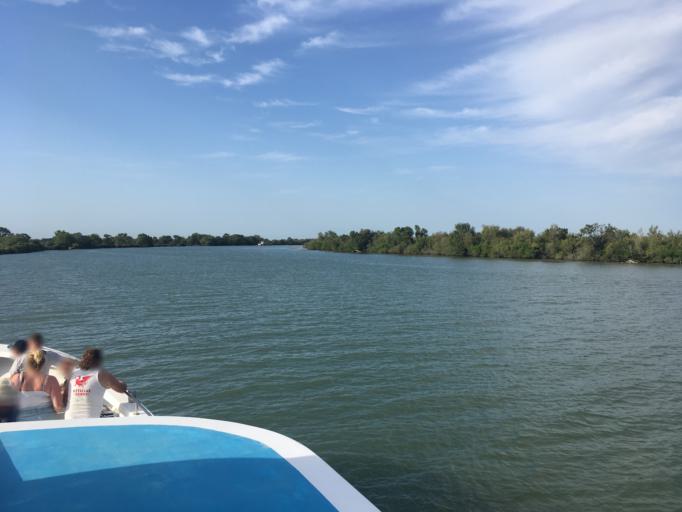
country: FR
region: Provence-Alpes-Cote d'Azur
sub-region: Departement des Bouches-du-Rhone
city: Saintes-Maries-de-la-Mer
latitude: 43.4777
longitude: 4.3767
